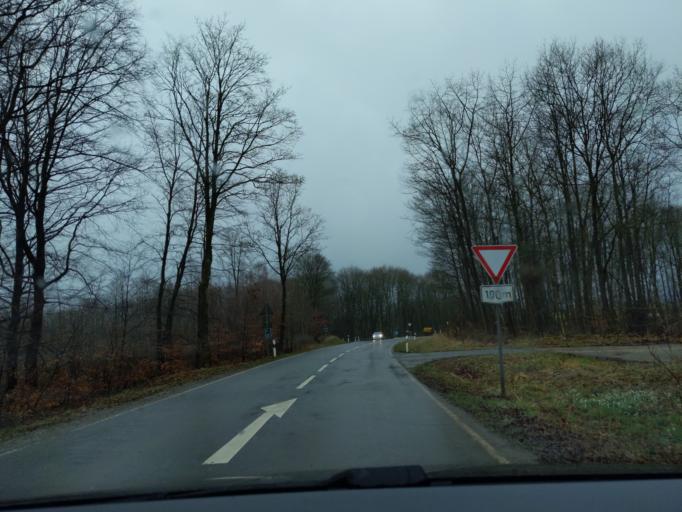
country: DE
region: Hesse
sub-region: Regierungsbezirk Kassel
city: Korbach
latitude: 51.2807
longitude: 8.9091
